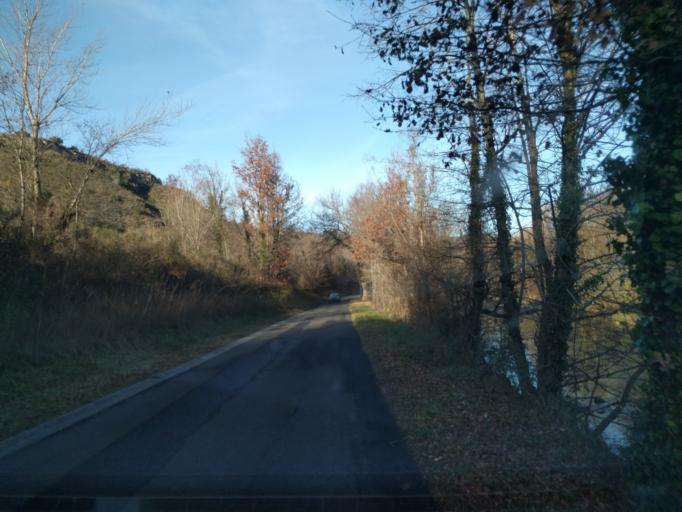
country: FR
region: Languedoc-Roussillon
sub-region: Departement de l'Aude
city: Quillan
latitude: 42.8983
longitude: 2.1858
